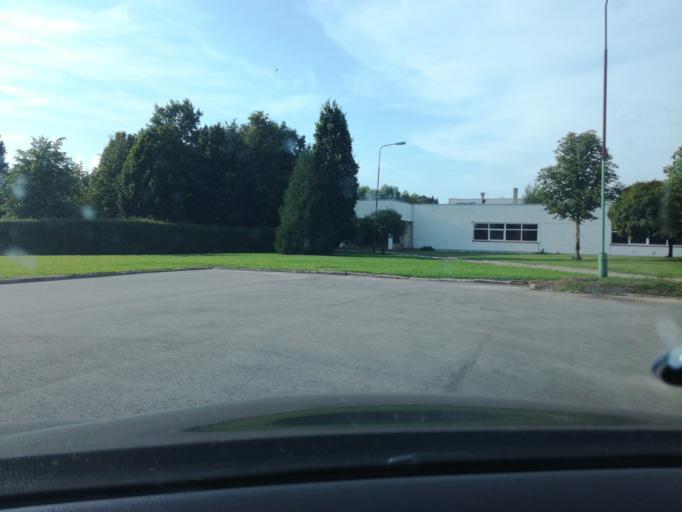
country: LT
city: Simnas
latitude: 54.3817
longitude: 23.6554
